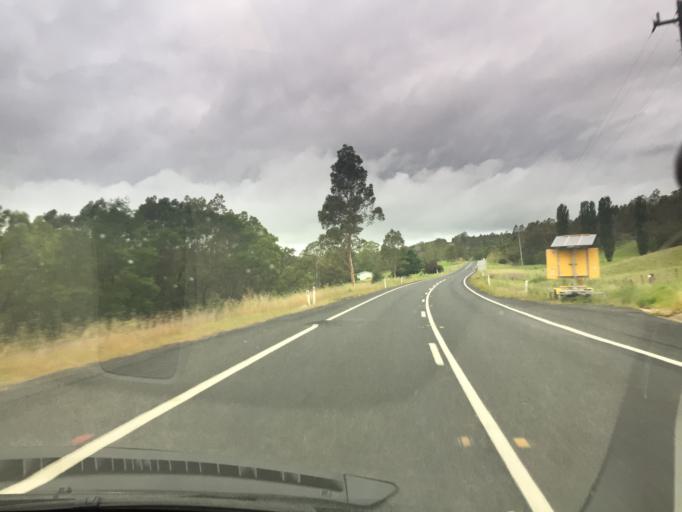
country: AU
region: New South Wales
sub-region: Bega Valley
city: Bega
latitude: -36.6142
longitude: 149.5032
